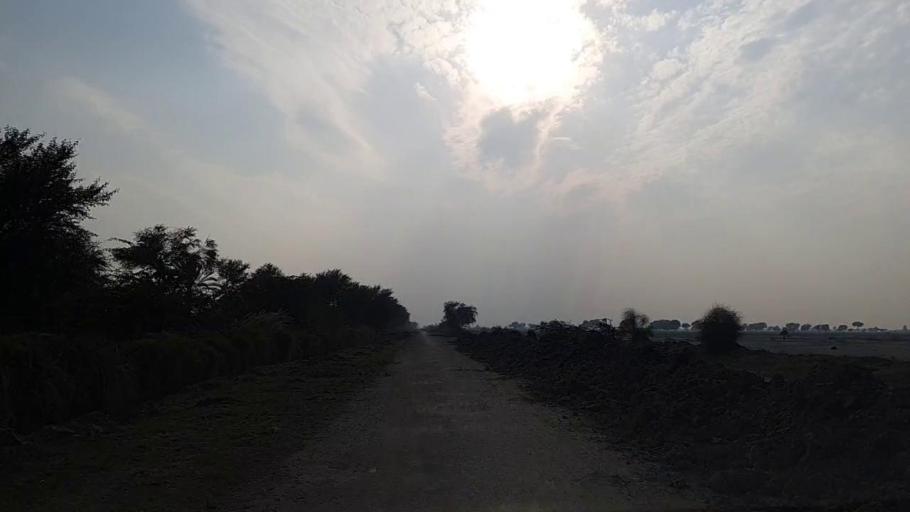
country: PK
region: Sindh
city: Jam Sahib
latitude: 26.3055
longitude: 68.5186
